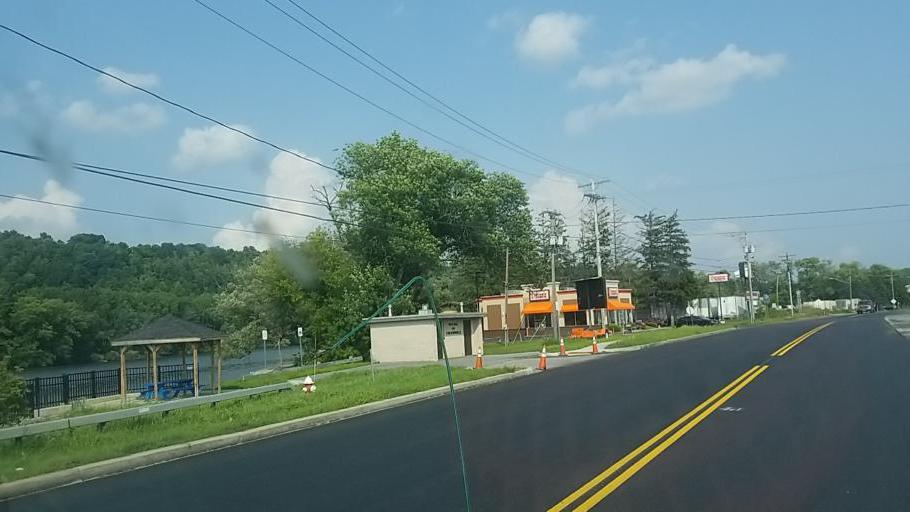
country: US
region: New York
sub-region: Montgomery County
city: Fonda
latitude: 42.9488
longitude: -74.3593
